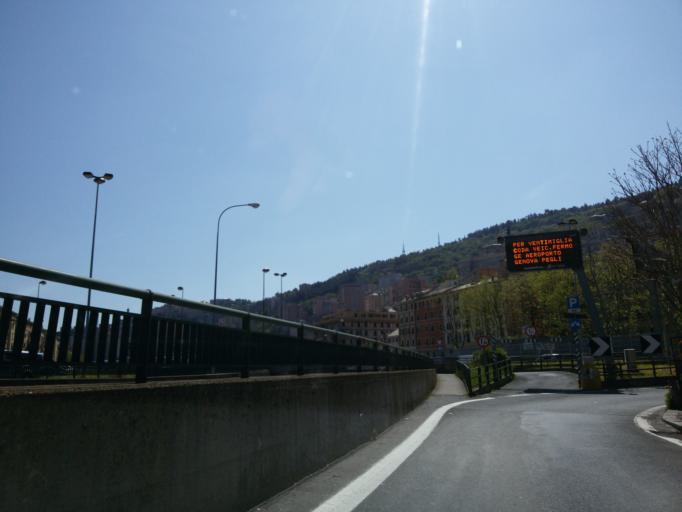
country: IT
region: Liguria
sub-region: Provincia di Genova
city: Genoa
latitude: 44.4271
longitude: 8.9484
